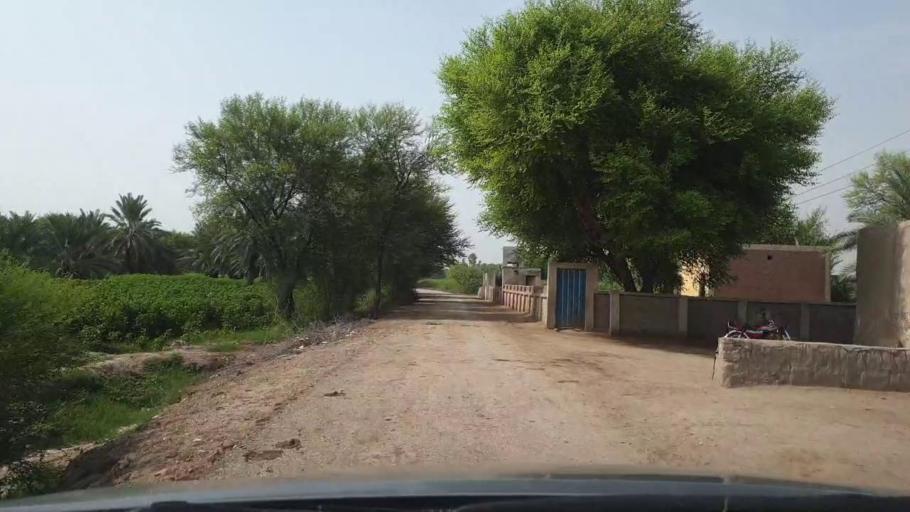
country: PK
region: Sindh
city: Rohri
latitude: 27.6581
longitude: 69.0117
